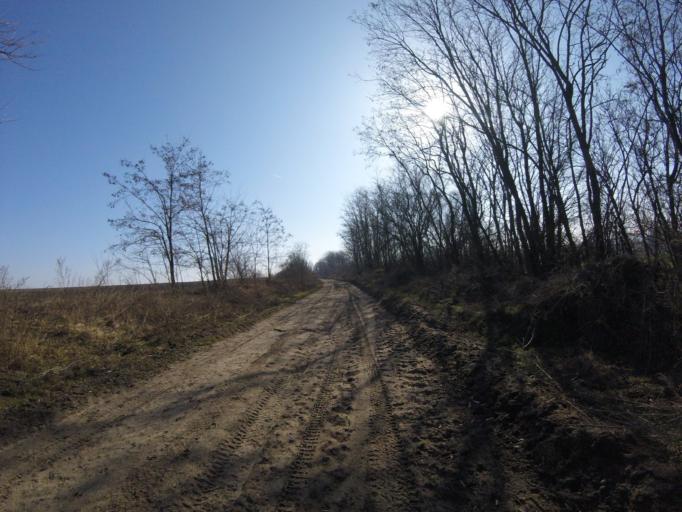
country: HU
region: Komarom-Esztergom
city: Bokod
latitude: 47.5285
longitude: 18.1994
